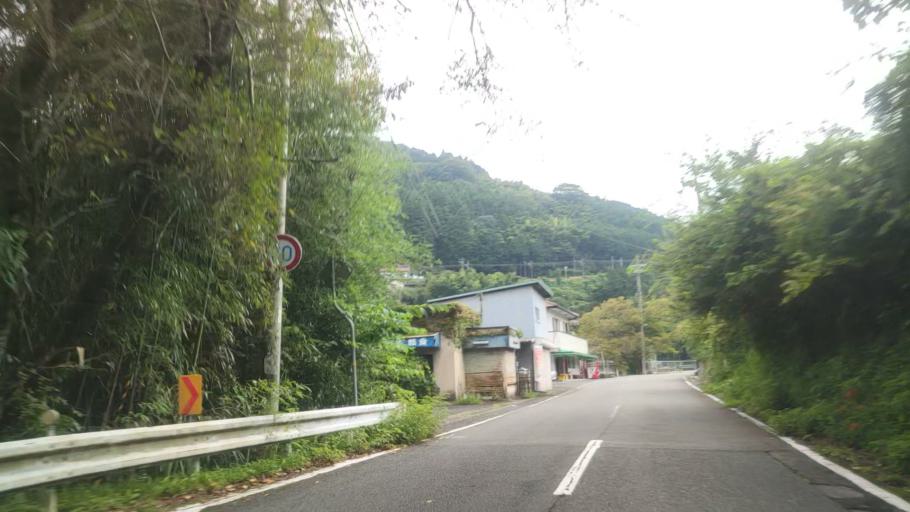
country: JP
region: Wakayama
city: Koya
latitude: 34.2594
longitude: 135.5469
